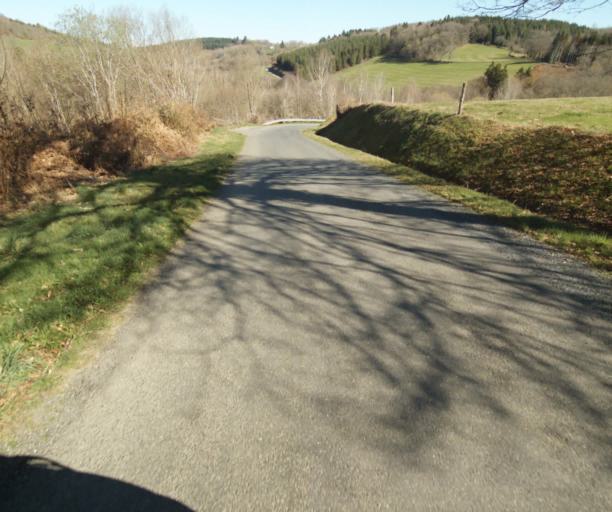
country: FR
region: Limousin
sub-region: Departement de la Correze
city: Seilhac
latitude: 45.3755
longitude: 1.7495
